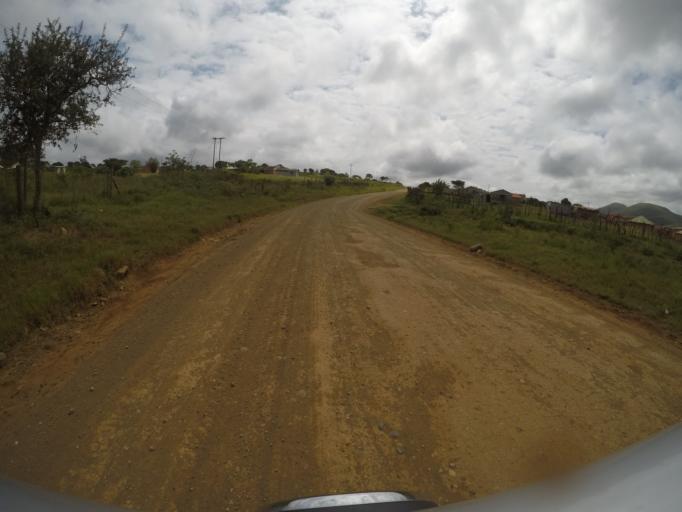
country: ZA
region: KwaZulu-Natal
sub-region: uThungulu District Municipality
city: Empangeni
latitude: -28.5820
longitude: 31.8459
